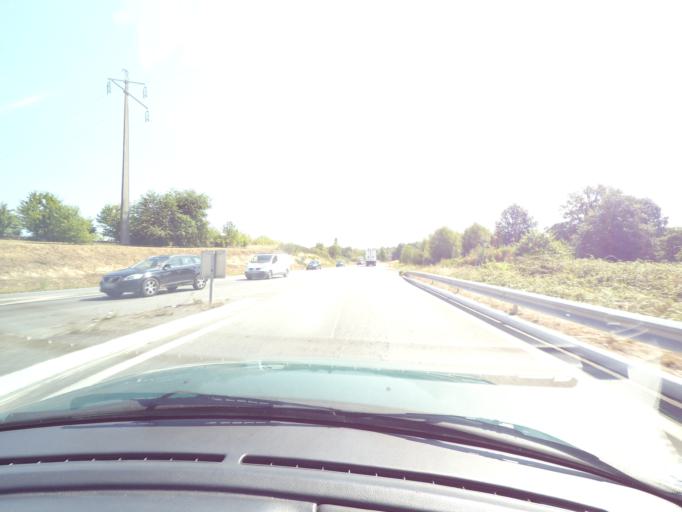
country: FR
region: Limousin
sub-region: Departement de la Haute-Vienne
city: Chaptelat
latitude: 45.8910
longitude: 1.2809
